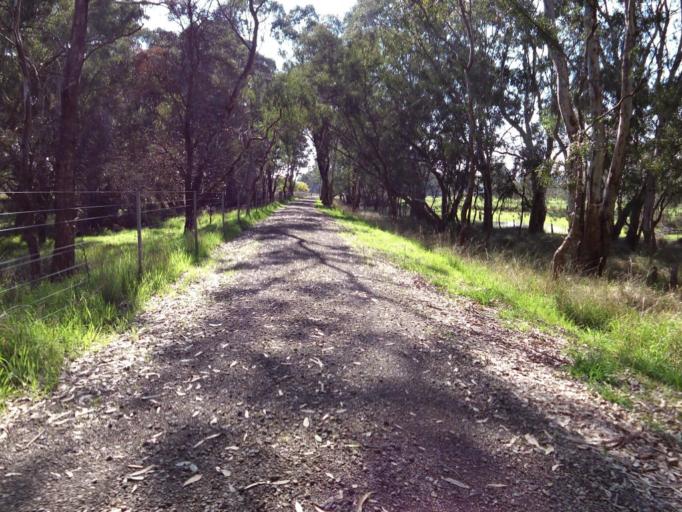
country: AU
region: Victoria
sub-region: Murrindindi
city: Alexandra
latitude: -37.1542
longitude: 145.5760
